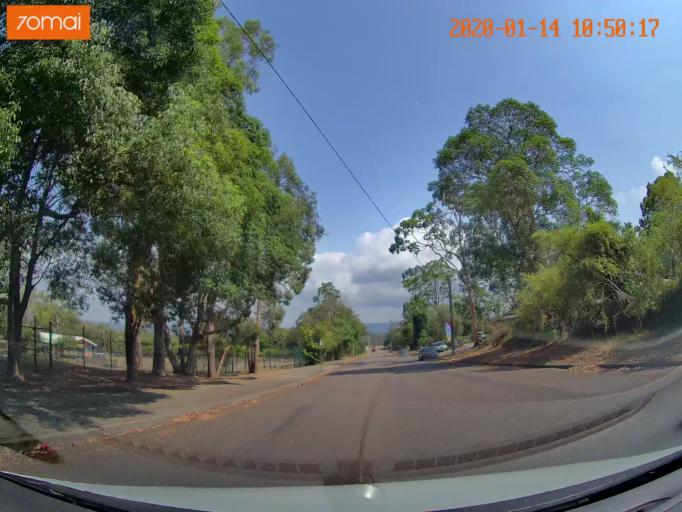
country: AU
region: New South Wales
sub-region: Lake Macquarie Shire
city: Dora Creek
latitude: -33.1042
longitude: 151.4877
